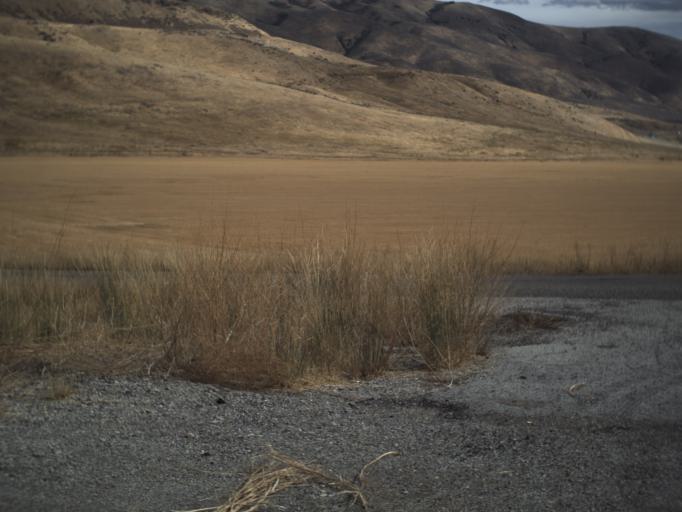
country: US
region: Utah
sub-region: Box Elder County
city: Garland
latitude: 41.8017
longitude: -112.3036
